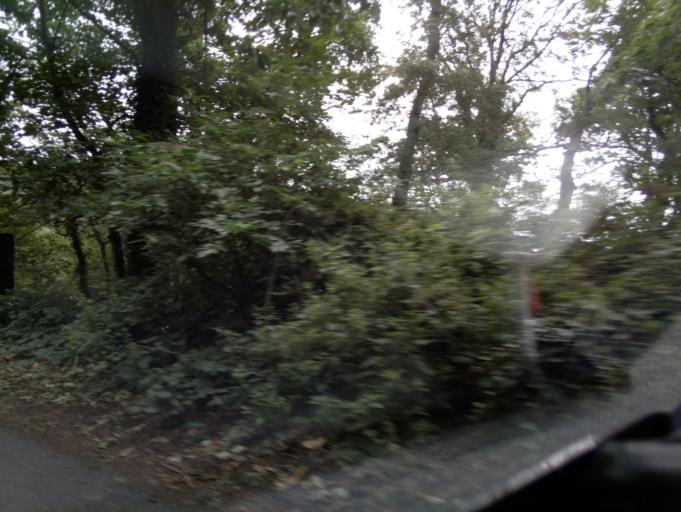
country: GB
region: England
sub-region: Devon
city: Dartmouth
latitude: 50.3170
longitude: -3.6137
